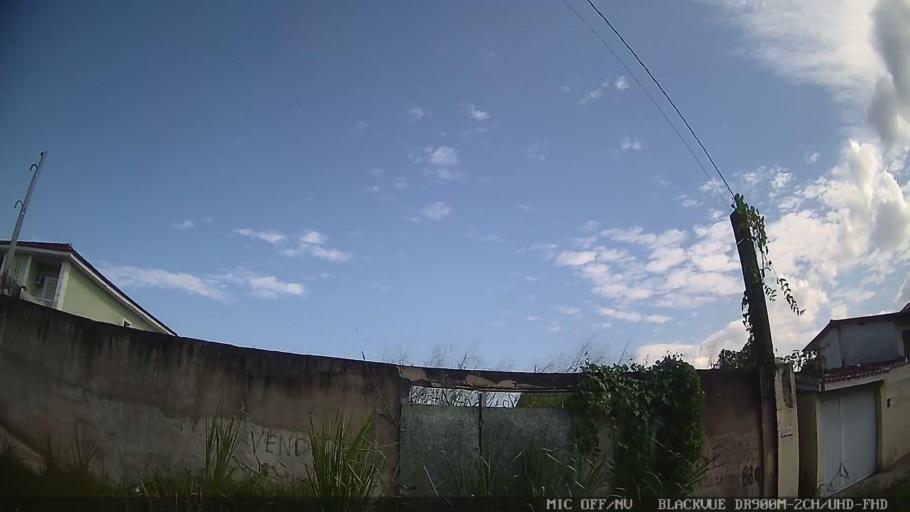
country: BR
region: Sao Paulo
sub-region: Guaruja
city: Guaruja
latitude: -23.9772
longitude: -46.2112
